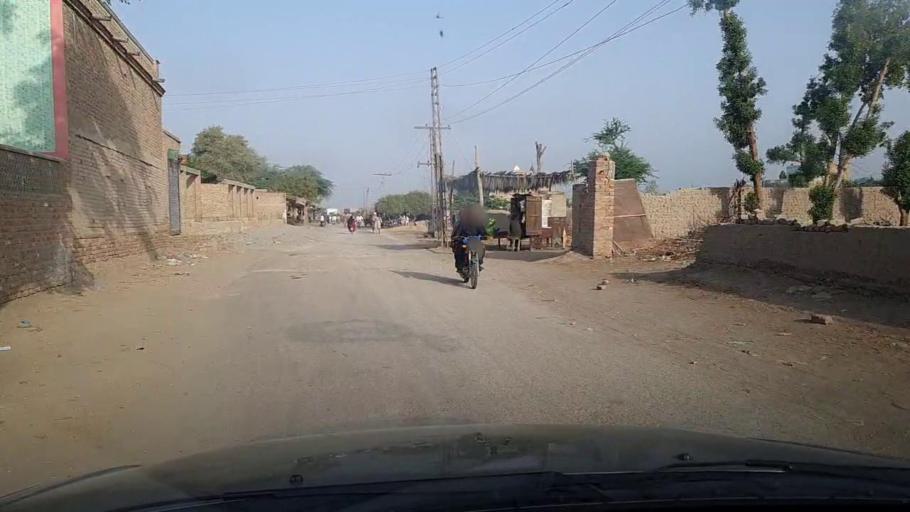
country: PK
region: Sindh
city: Pir jo Goth
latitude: 27.5582
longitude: 68.6740
